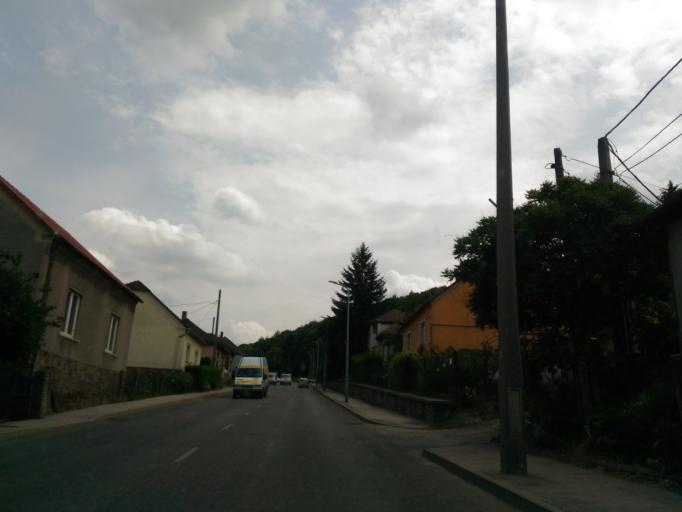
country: HU
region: Baranya
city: Komlo
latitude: 46.1889
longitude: 18.2592
